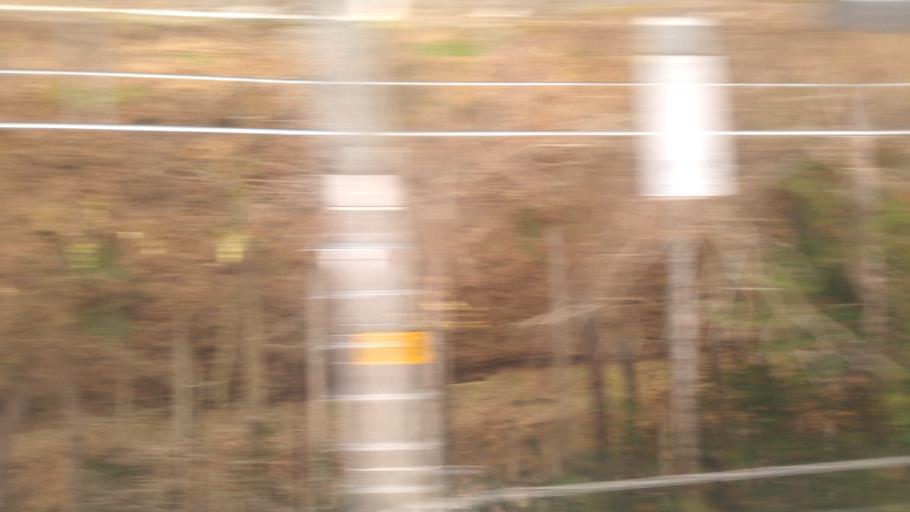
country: JP
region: Nagano
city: Ina
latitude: 35.8866
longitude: 137.7625
